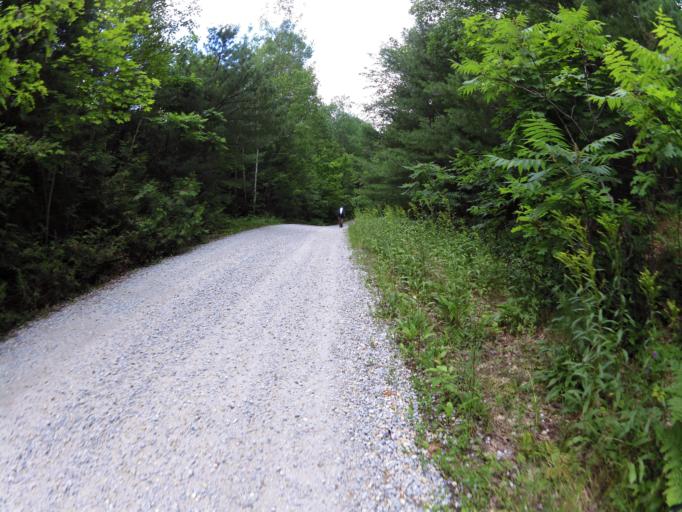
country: CA
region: Ontario
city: Perth
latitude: 45.0107
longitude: -76.5939
